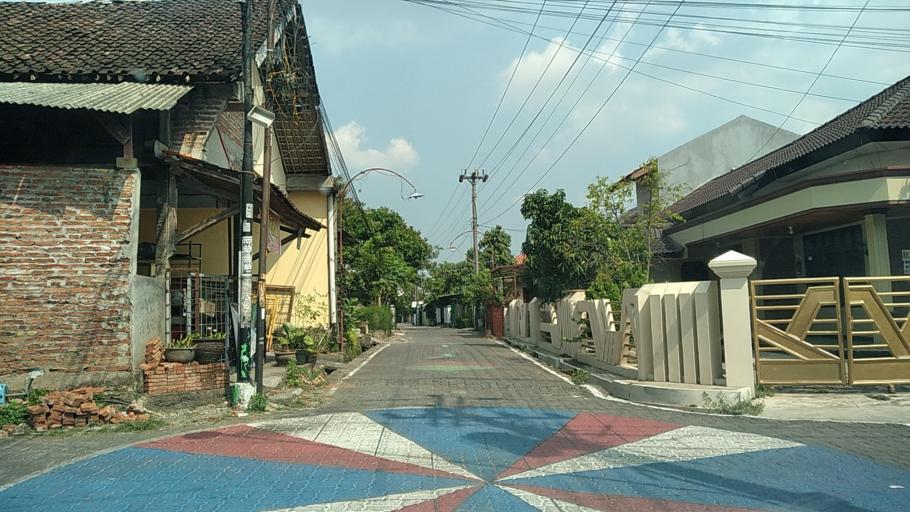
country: ID
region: Central Java
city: Semarang
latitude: -7.0479
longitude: 110.4217
